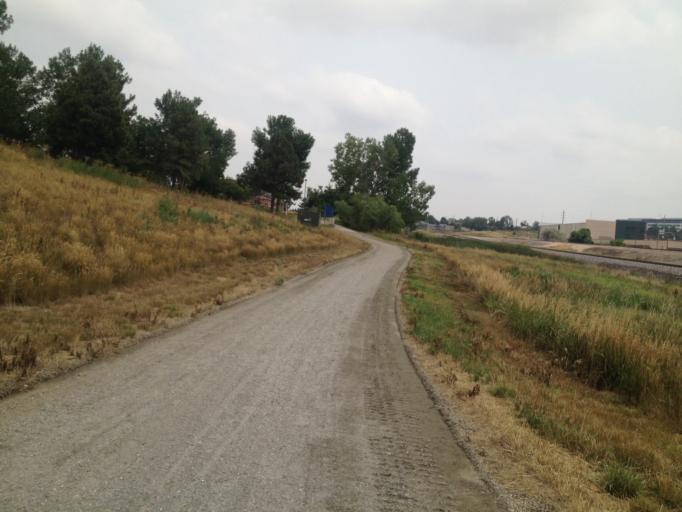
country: US
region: Colorado
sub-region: Broomfield County
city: Broomfield
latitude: 39.9267
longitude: -105.1098
